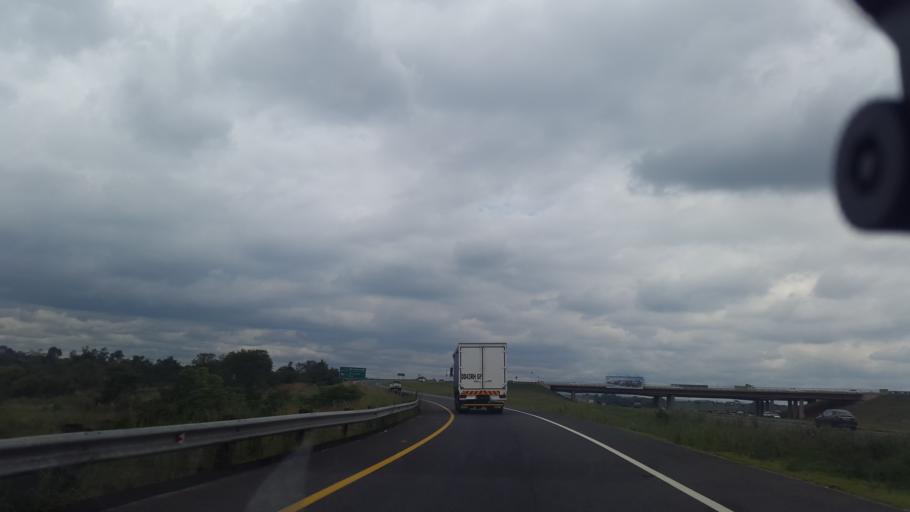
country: ZA
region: Gauteng
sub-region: West Rand District Municipality
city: Muldersdriseloop
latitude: -25.9848
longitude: 27.9229
